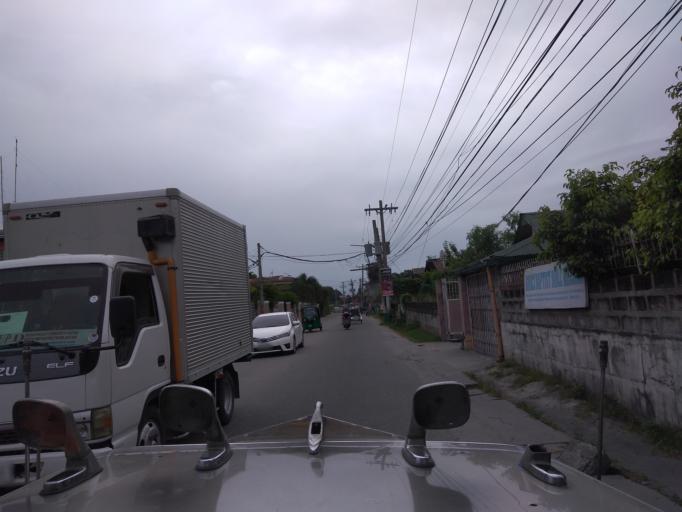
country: PH
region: Central Luzon
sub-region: Province of Pampanga
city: Mexico
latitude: 15.0618
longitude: 120.7180
